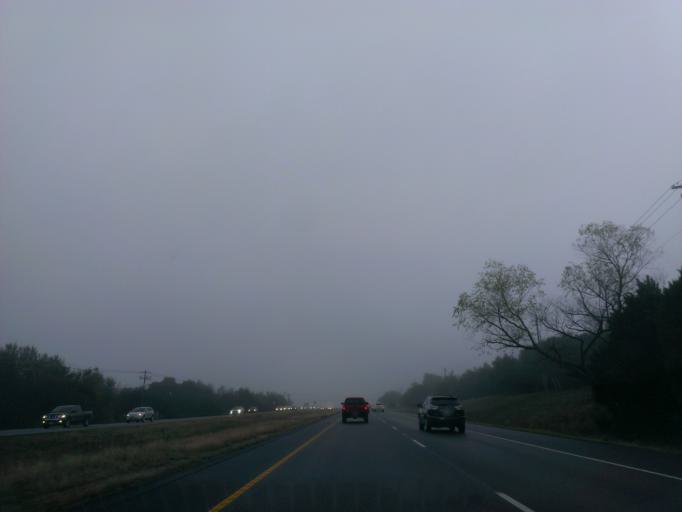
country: US
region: Texas
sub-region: Williamson County
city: Jollyville
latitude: 30.3731
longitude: -97.7839
